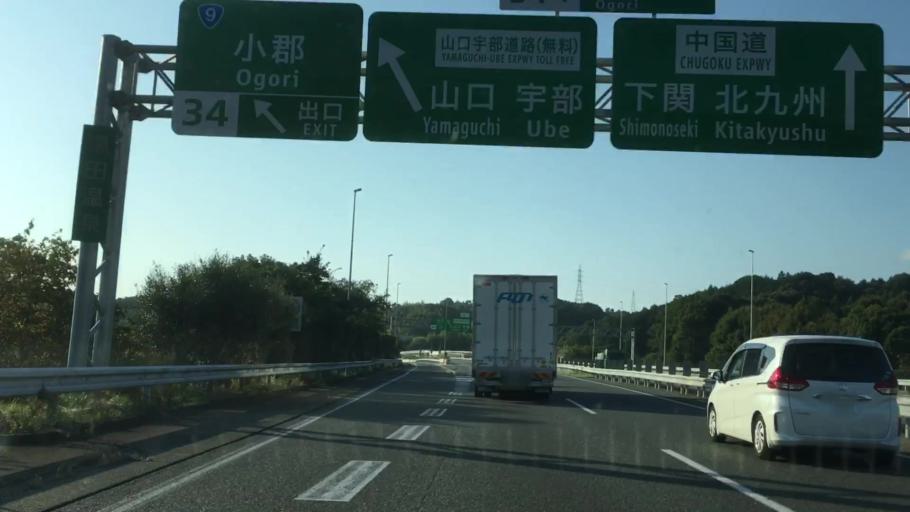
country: JP
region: Yamaguchi
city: Ogori-shimogo
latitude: 34.1252
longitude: 131.4071
